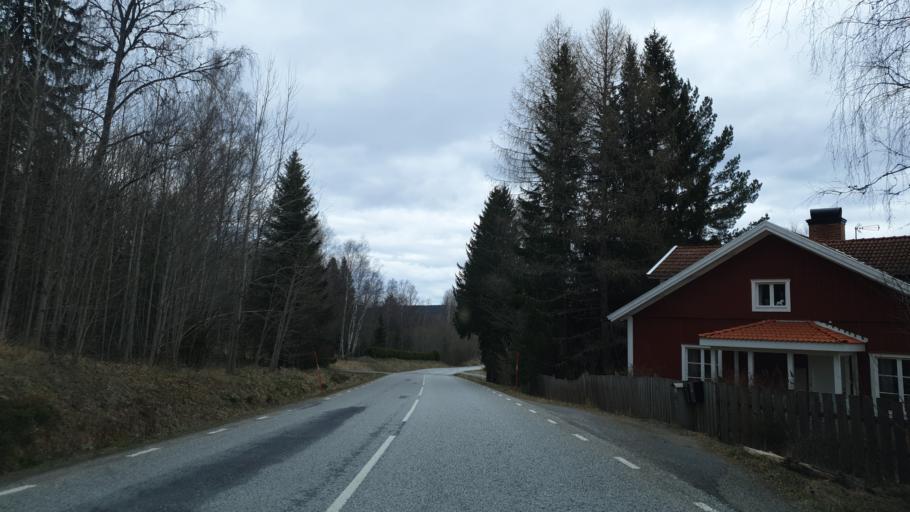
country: SE
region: OErebro
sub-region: Nora Kommun
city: As
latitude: 59.6025
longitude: 14.9250
